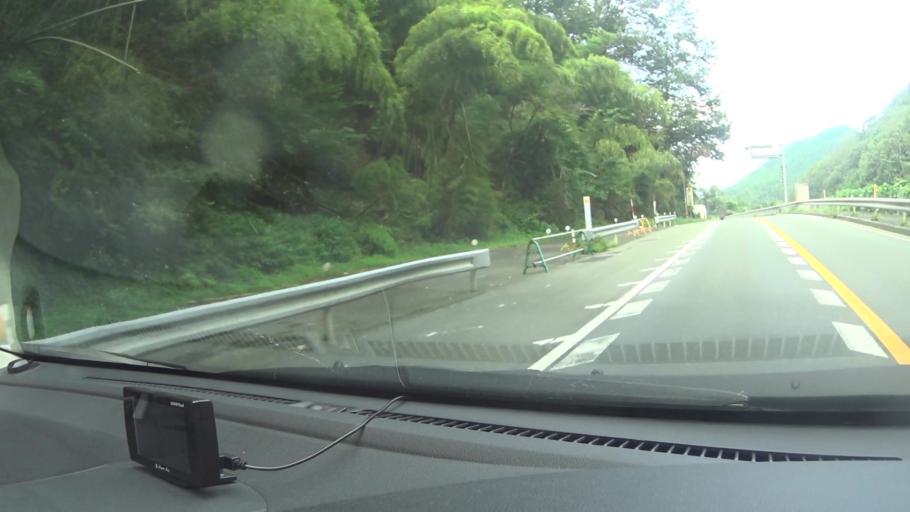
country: JP
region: Kyoto
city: Ayabe
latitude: 35.2413
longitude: 135.3155
